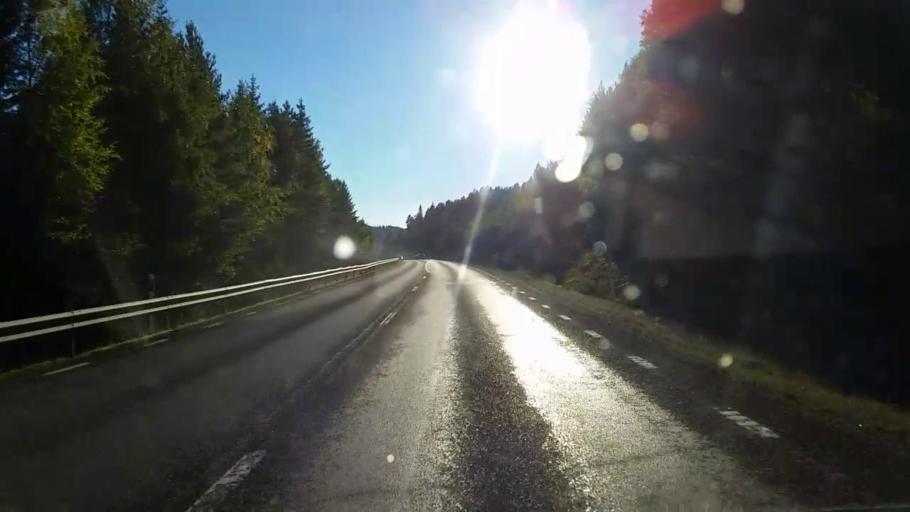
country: SE
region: Gaevleborg
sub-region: Hudiksvalls Kommun
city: Delsbo
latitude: 61.8008
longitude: 16.3614
